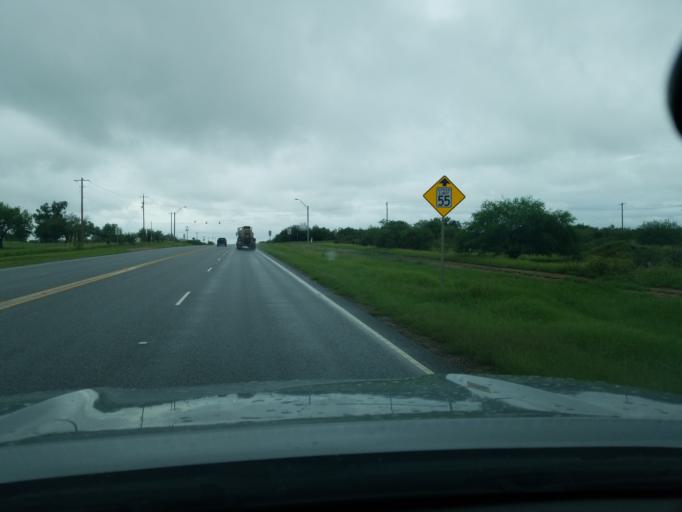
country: US
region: Texas
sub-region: Dimmit County
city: Carrizo Springs
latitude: 28.5299
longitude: -99.8321
